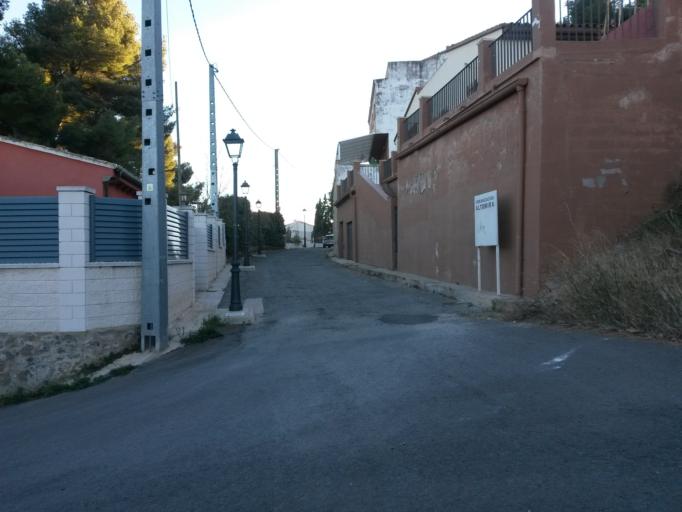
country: ES
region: Valencia
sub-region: Provincia de Castello
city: Navajas
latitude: 39.8735
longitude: -0.5083
